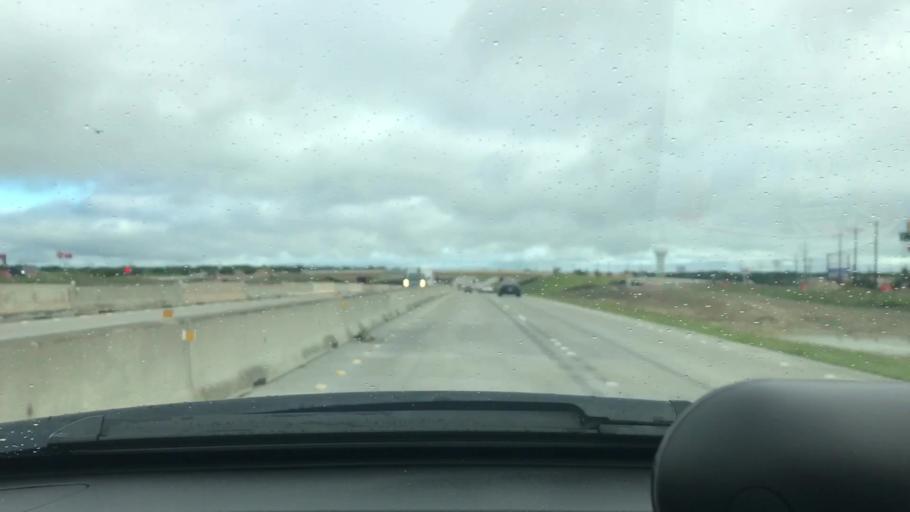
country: US
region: Texas
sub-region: Collin County
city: Anna
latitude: 33.3424
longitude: -96.5869
